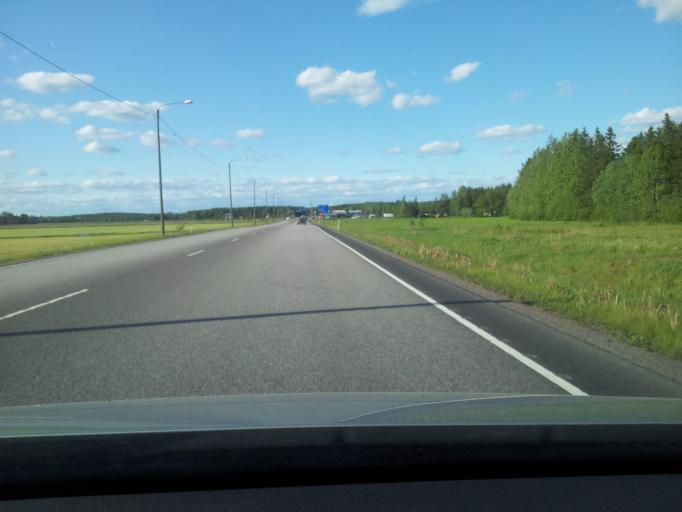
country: FI
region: Uusimaa
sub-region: Loviisa
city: Lapinjaervi
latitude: 60.6657
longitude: 26.2476
